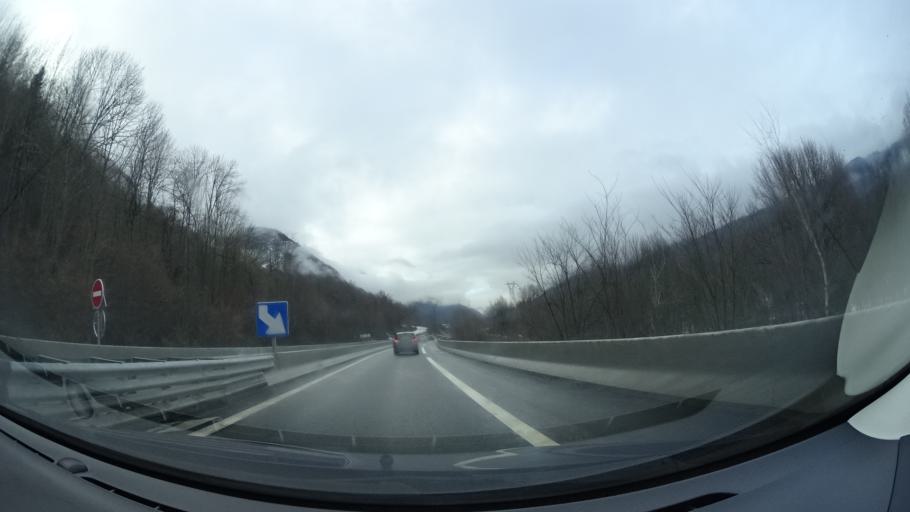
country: FR
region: Midi-Pyrenees
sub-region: Departement de l'Ariege
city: Ax-les-Thermes
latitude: 42.7262
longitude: 1.8103
